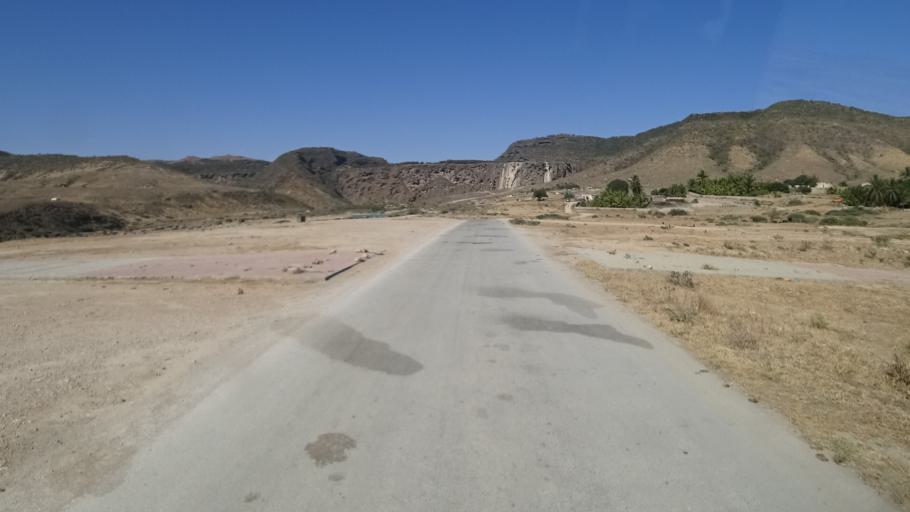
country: OM
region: Zufar
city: Salalah
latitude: 17.0634
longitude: 54.4307
